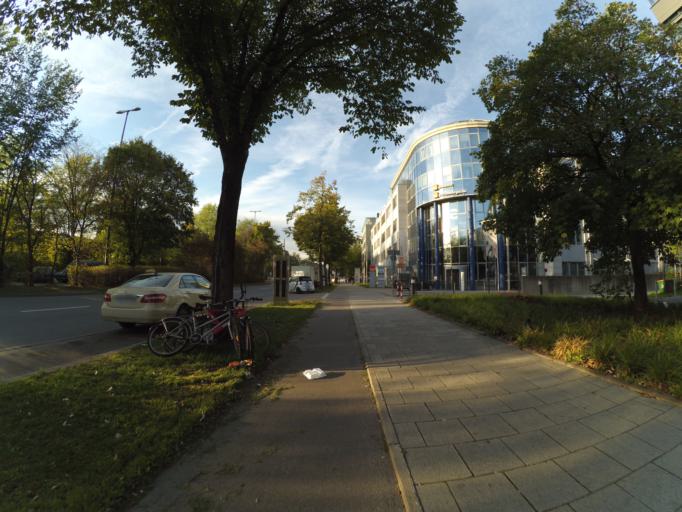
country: DE
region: Bavaria
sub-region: Upper Bavaria
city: Bogenhausen
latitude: 48.1831
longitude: 11.5850
